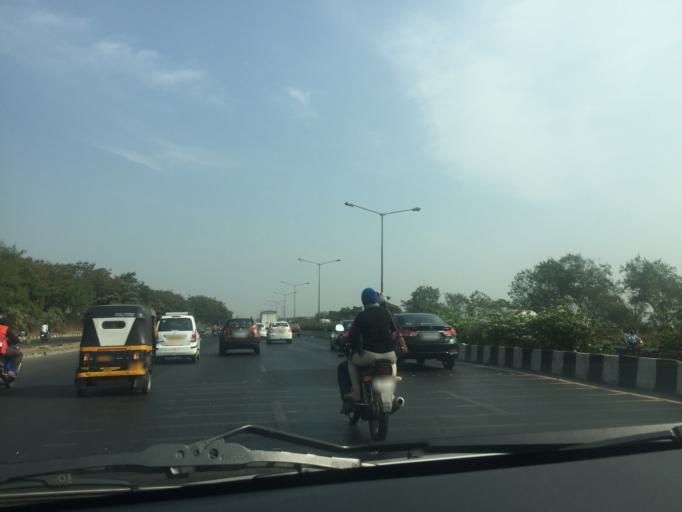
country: IN
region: Maharashtra
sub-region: Mumbai Suburban
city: Powai
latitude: 19.1394
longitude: 72.9472
